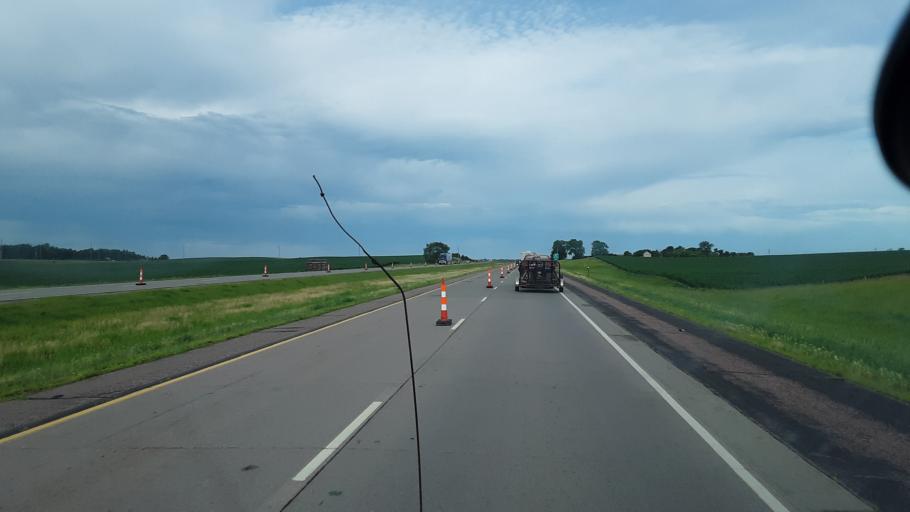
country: US
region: South Dakota
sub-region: Minnehaha County
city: Crooks
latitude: 43.6087
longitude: -96.8610
